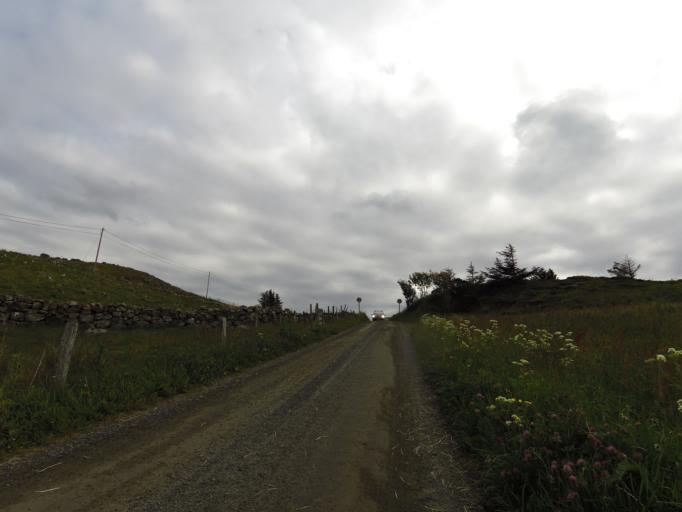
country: NO
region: Vest-Agder
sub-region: Farsund
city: Vestbygd
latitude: 58.1413
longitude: 6.6108
